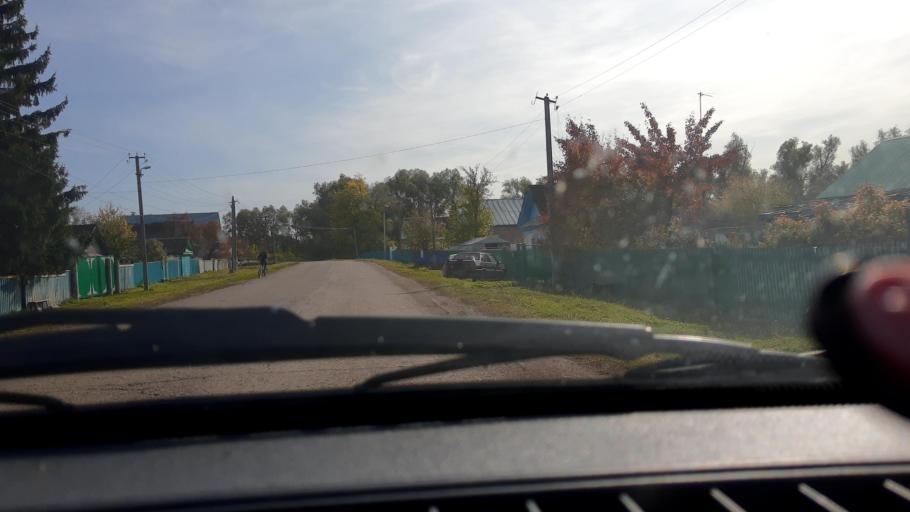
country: RU
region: Bashkortostan
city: Chekmagush
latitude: 54.8809
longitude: 54.6062
